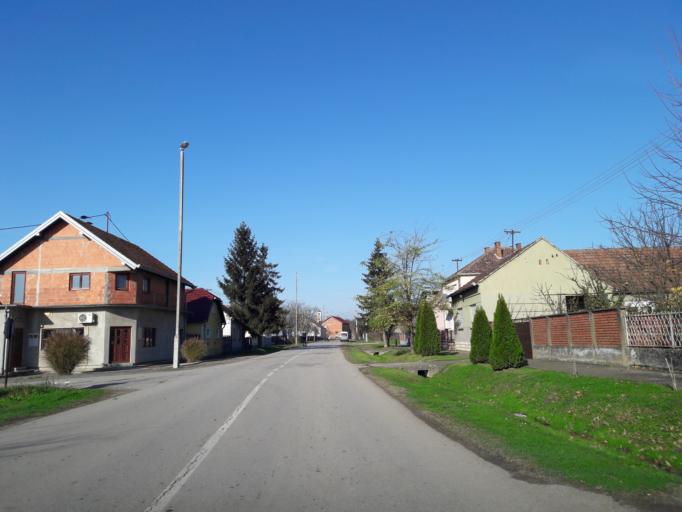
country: HR
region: Vukovarsko-Srijemska
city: Vodinci
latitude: 45.2726
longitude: 18.6109
